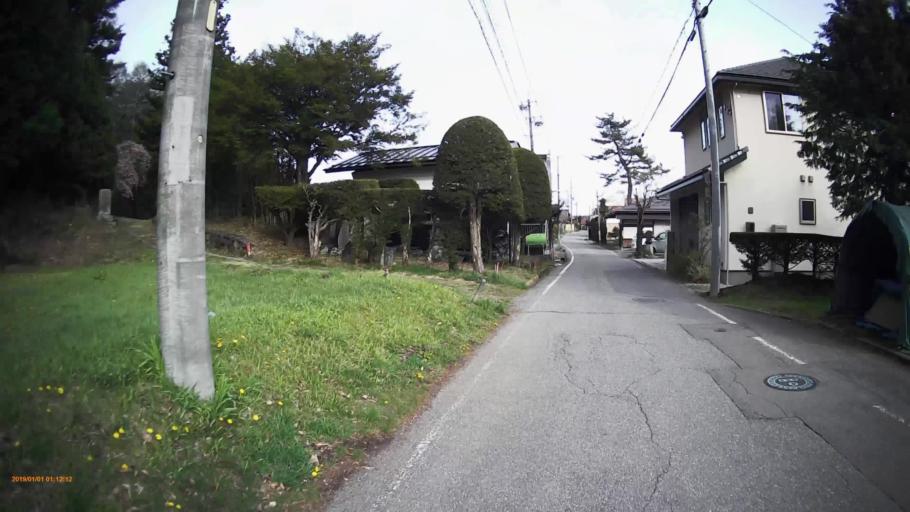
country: JP
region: Nagano
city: Chino
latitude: 35.9133
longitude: 138.2212
